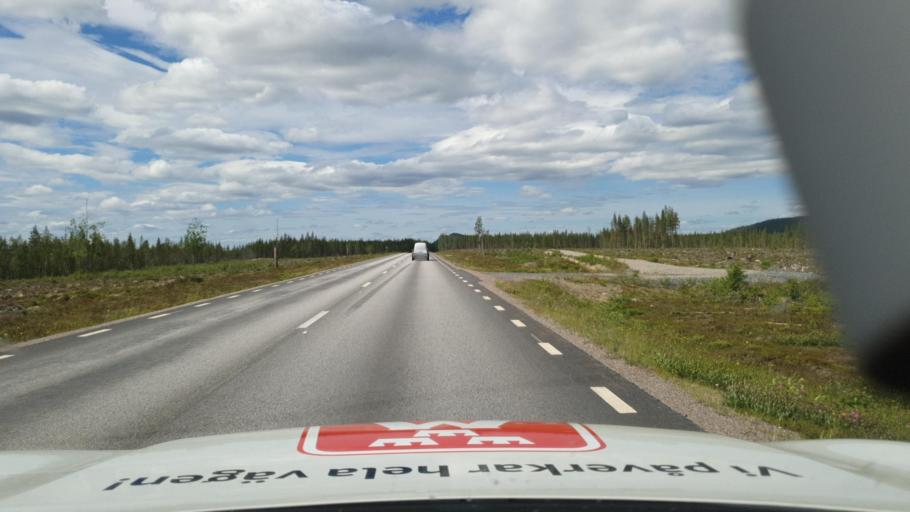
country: SE
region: Vaesterbotten
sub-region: Skelleftea Kommun
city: Langsele
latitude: 65.1251
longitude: 19.9376
